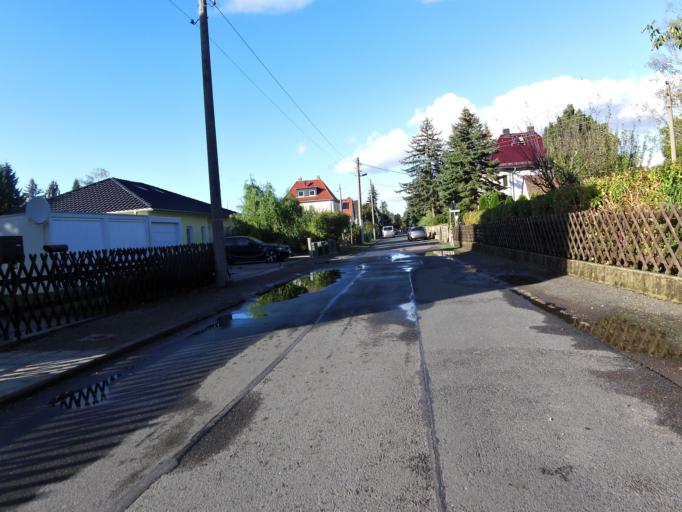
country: DE
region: Saxony
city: Taucha
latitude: 51.3253
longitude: 12.4760
